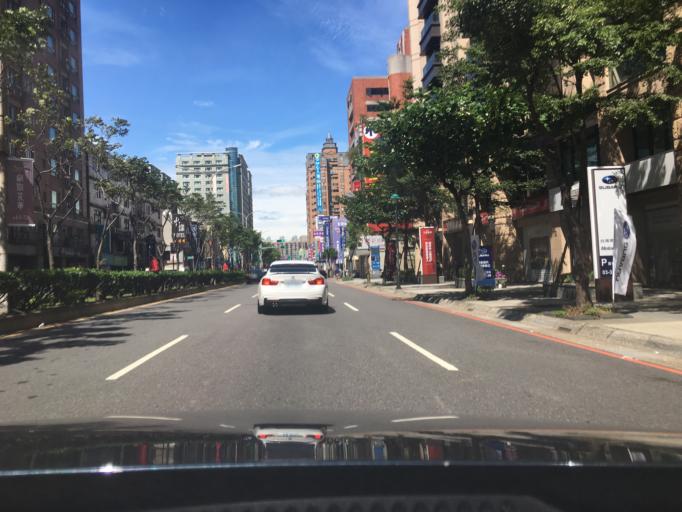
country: TW
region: Taiwan
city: Taoyuan City
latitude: 25.0450
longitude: 121.2935
